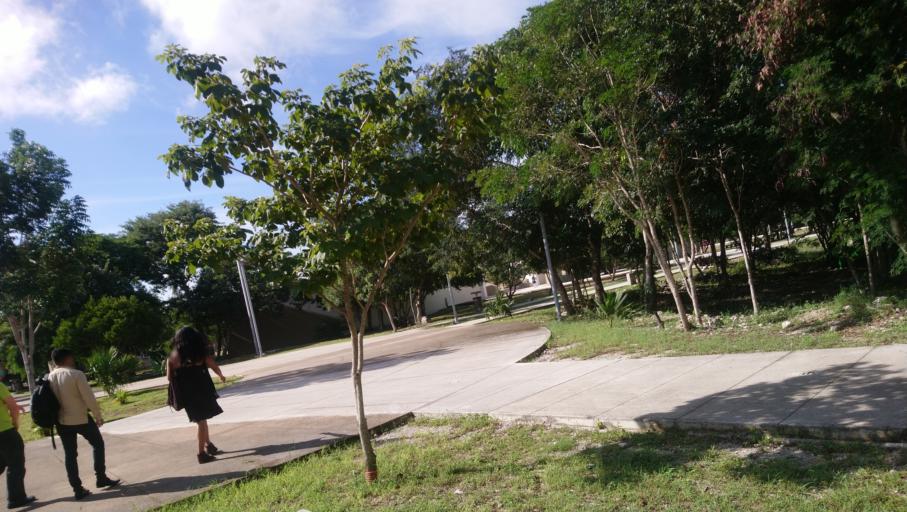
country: MX
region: Yucatan
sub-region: Merida
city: Sierra Papacal
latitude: 21.1304
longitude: -89.7810
